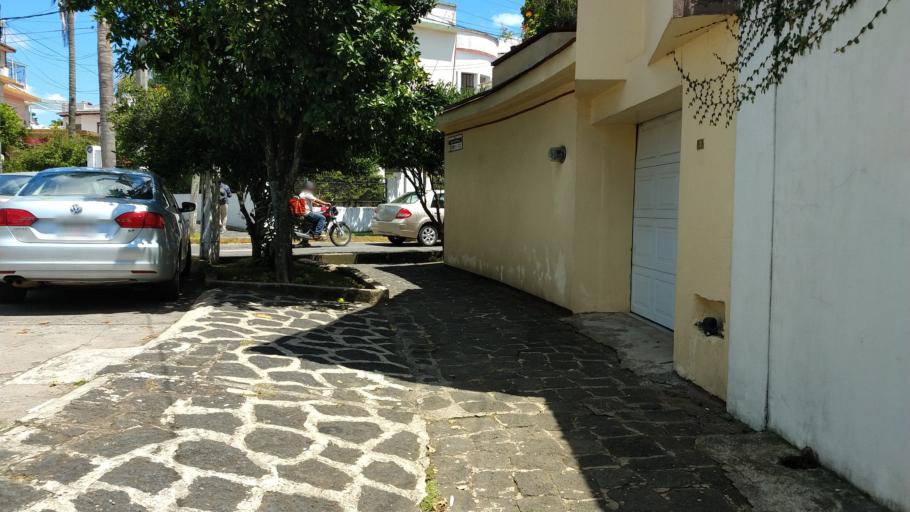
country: MX
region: Veracruz
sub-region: Xalapa
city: Xalapa de Enriquez
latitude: 19.5393
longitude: -96.9287
